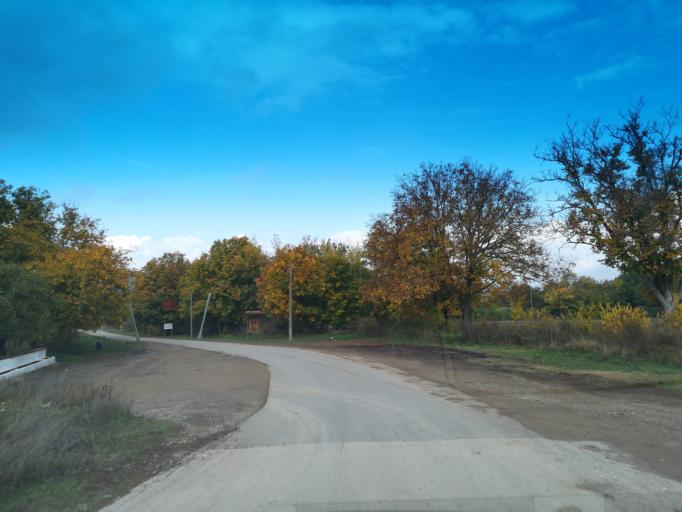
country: BG
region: Stara Zagora
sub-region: Obshtina Nikolaevo
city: Elkhovo
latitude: 42.3383
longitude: 25.4065
